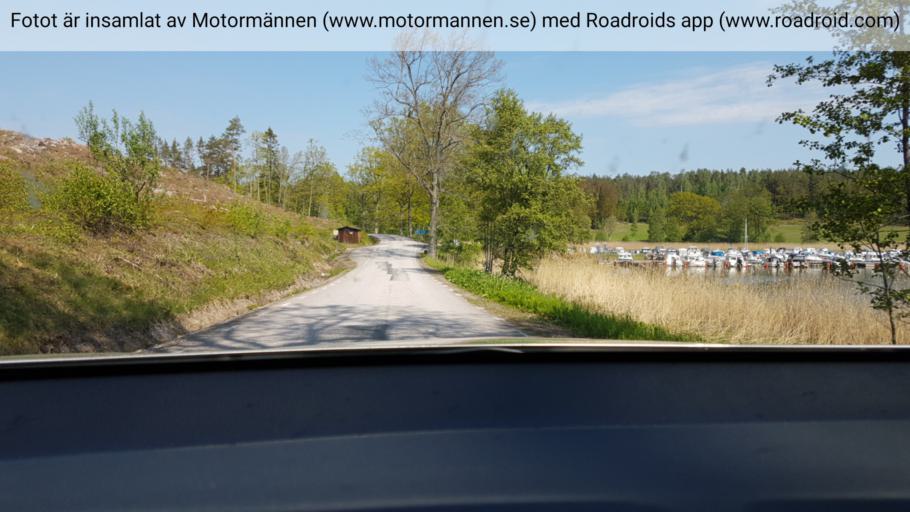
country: SE
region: Kalmar
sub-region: Vasterviks Kommun
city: Vaestervik
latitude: 57.8380
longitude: 16.5414
